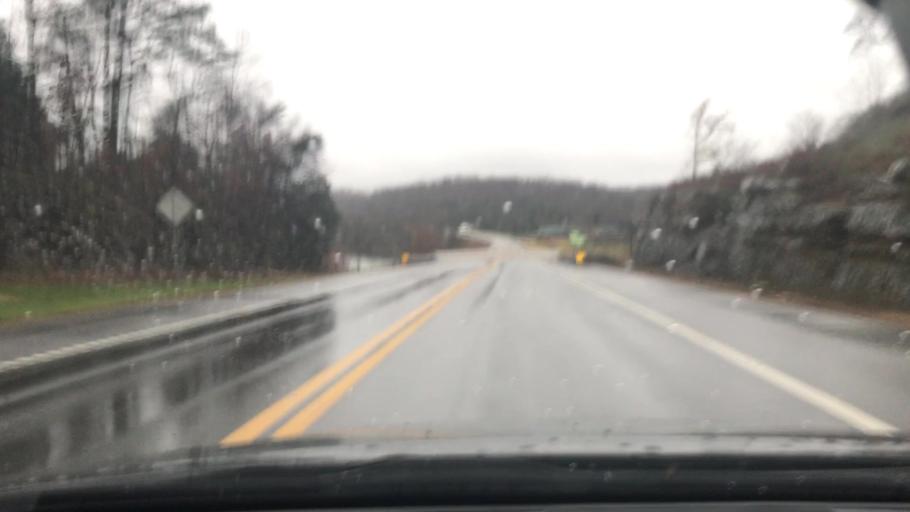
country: US
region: Tennessee
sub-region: Cheatham County
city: Ashland City
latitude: 36.2867
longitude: -87.1470
